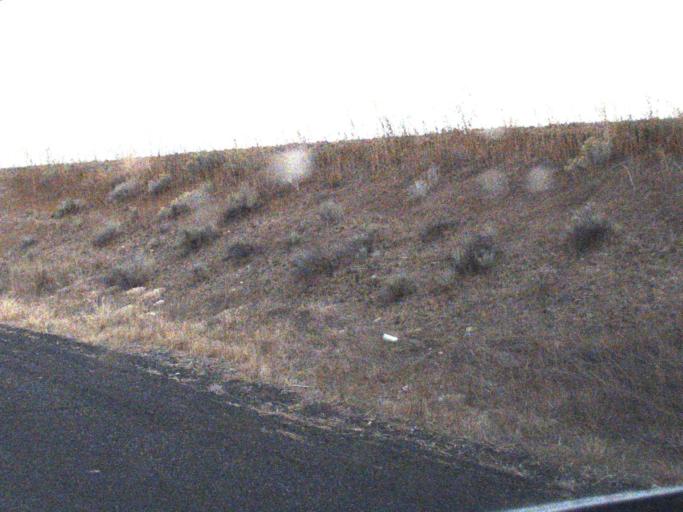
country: US
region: Washington
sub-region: Adams County
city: Ritzville
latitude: 46.7955
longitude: -118.4858
